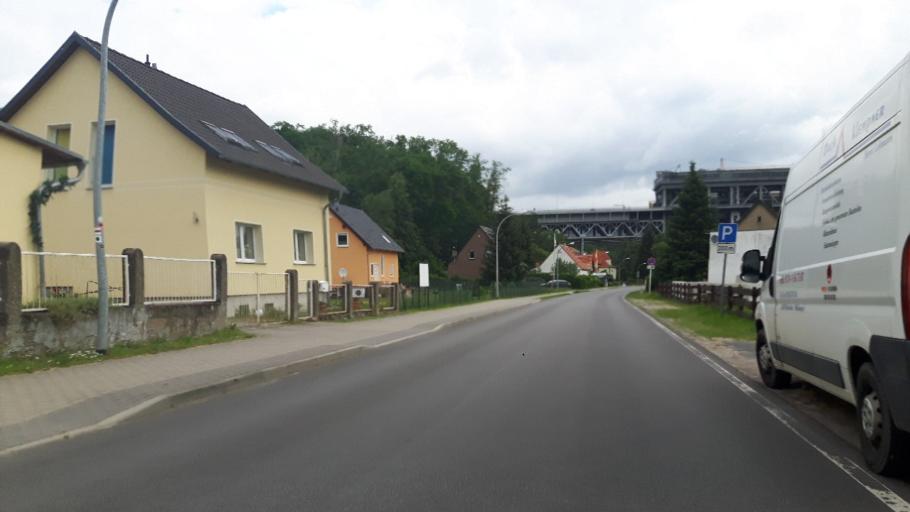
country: DE
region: Brandenburg
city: Niederfinow
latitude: 52.8461
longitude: 13.9390
